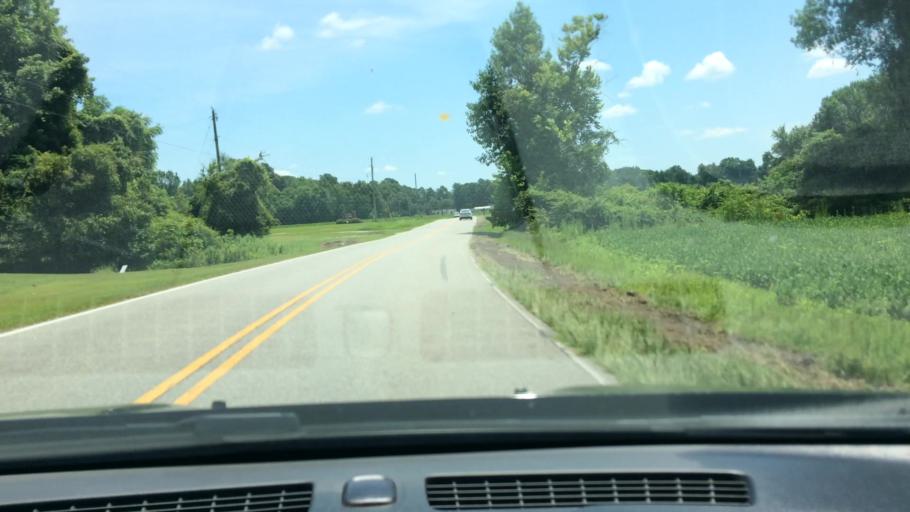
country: US
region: North Carolina
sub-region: Pitt County
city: Windsor
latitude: 35.5676
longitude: -77.2167
